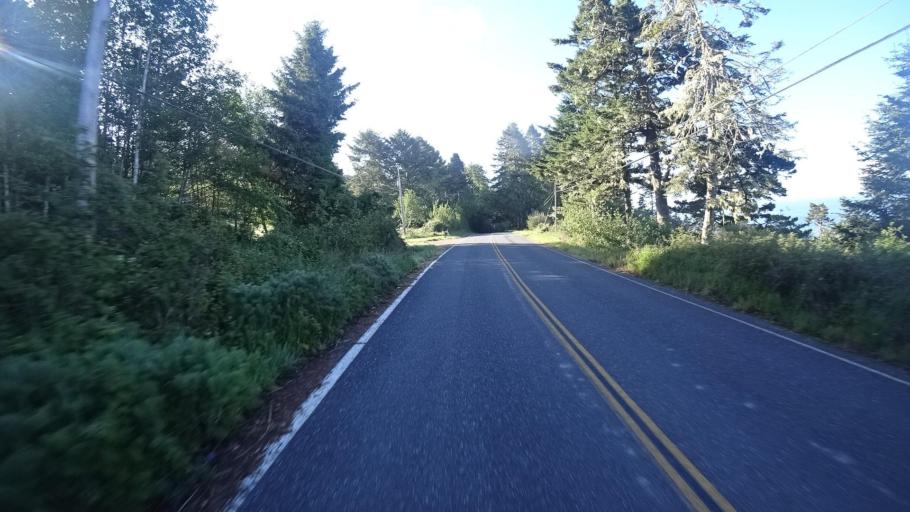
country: US
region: California
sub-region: Humboldt County
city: Westhaven-Moonstone
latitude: 41.0995
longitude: -124.1583
